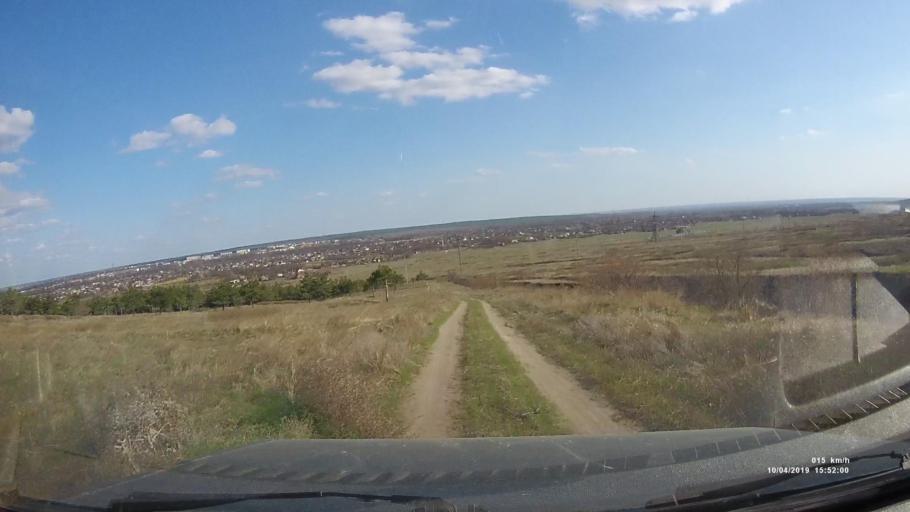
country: RU
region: Rostov
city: Masalovka
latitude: 48.4209
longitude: 40.2557
